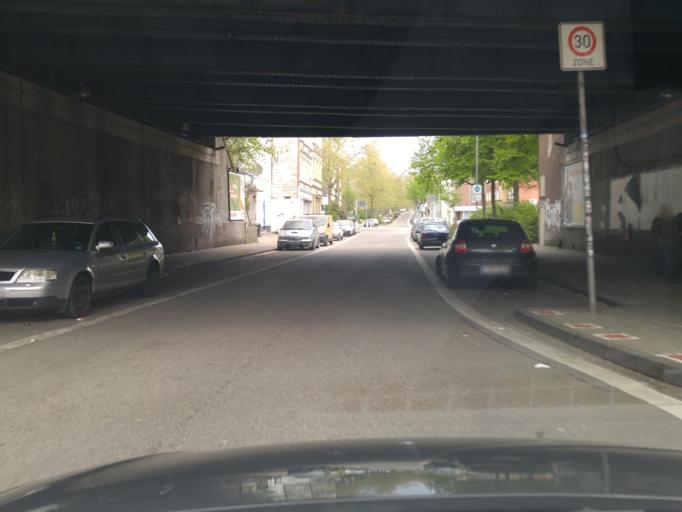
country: DE
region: North Rhine-Westphalia
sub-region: Regierungsbezirk Dusseldorf
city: Essen
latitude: 51.4626
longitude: 7.0137
